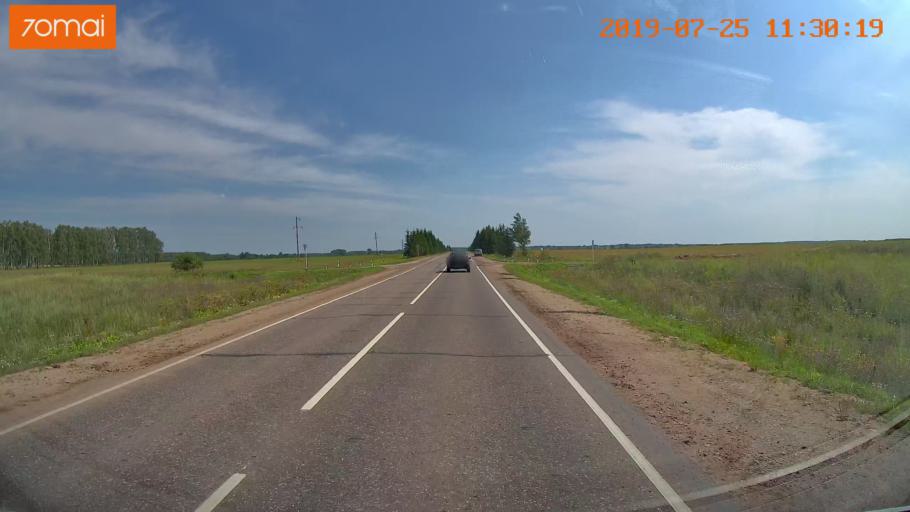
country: RU
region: Ivanovo
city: Privolzhsk
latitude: 57.3867
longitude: 41.3212
